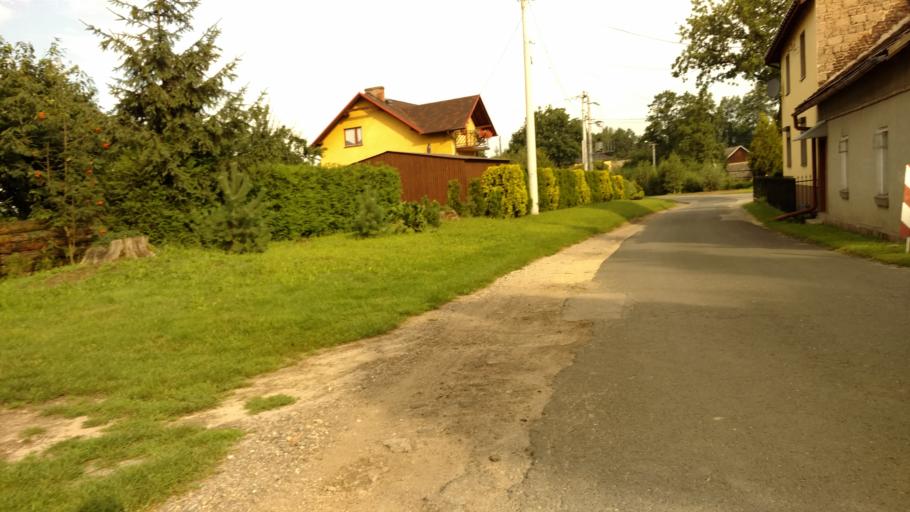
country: PL
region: Silesian Voivodeship
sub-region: Powiat pszczynski
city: Jankowice
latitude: 49.9987
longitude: 19.0016
